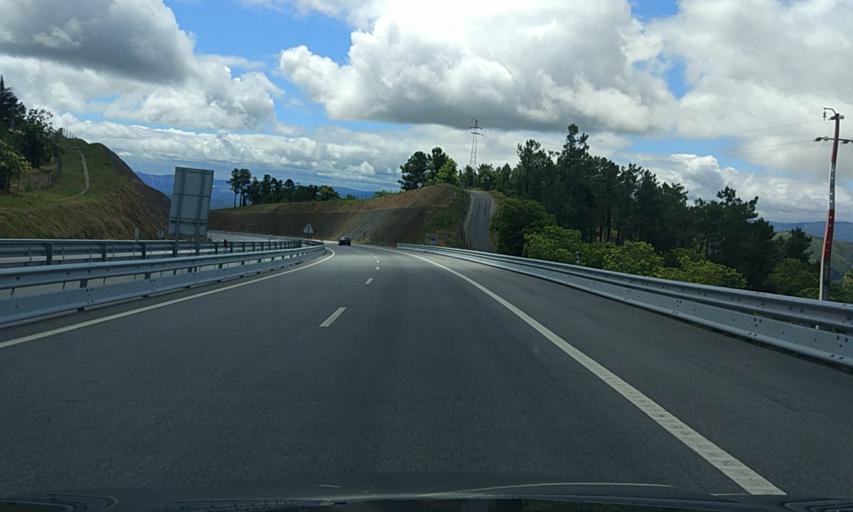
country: PT
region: Vila Real
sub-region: Santa Marta de Penaguiao
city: Santa Marta de Penaguiao
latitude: 41.2715
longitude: -7.8152
